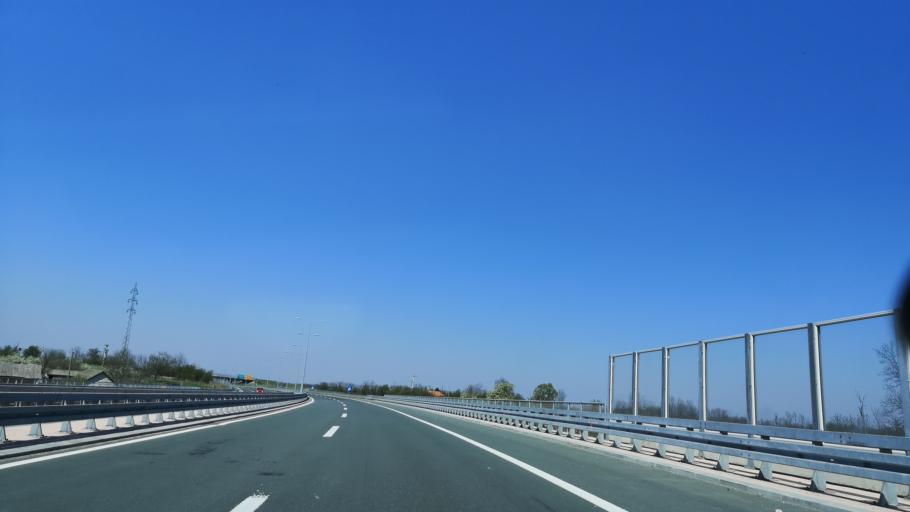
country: RS
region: Central Serbia
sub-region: Kolubarski Okrug
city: Ub
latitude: 44.4493
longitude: 20.1251
